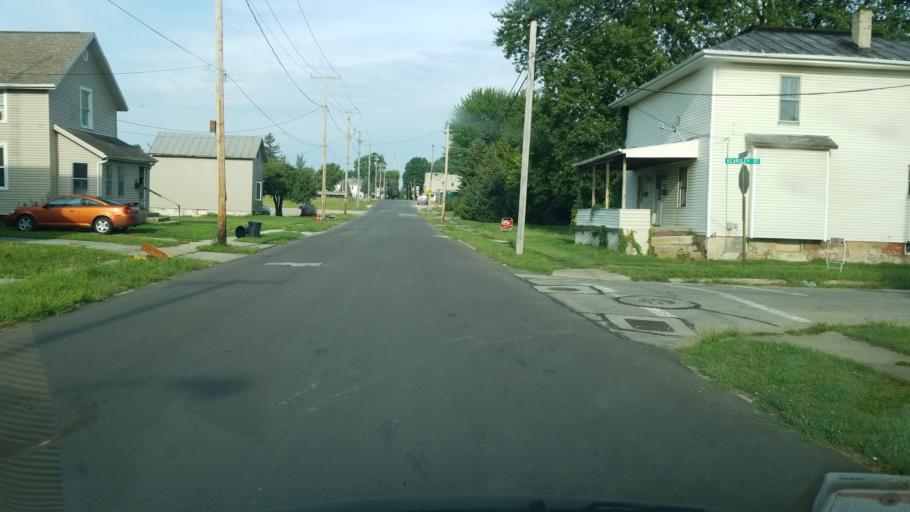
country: US
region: Ohio
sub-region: Crawford County
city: Bucyrus
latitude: 40.8050
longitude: -82.9643
